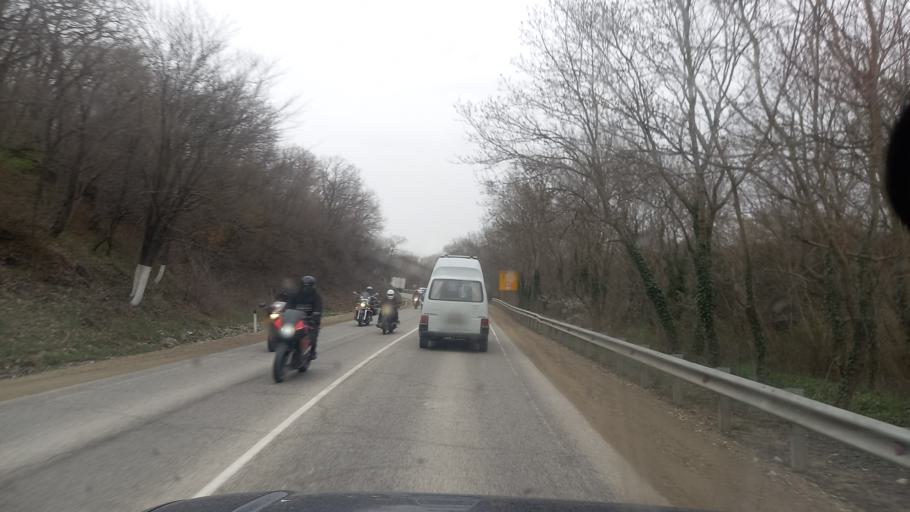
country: RU
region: Krasnodarskiy
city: Gayduk
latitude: 44.7394
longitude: 37.6792
